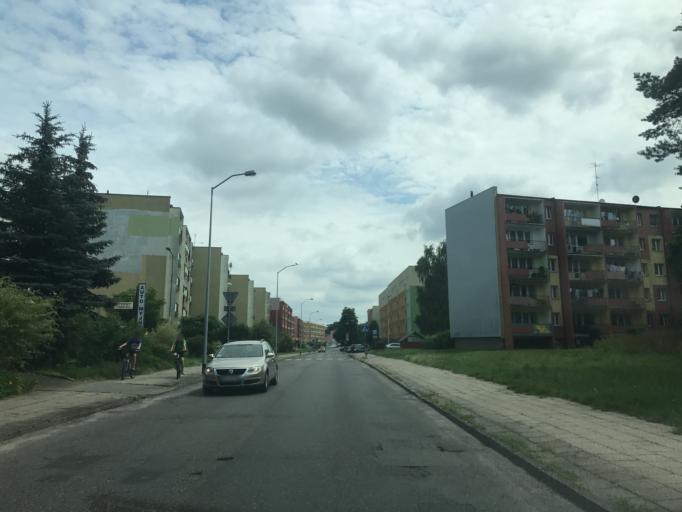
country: PL
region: West Pomeranian Voivodeship
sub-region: Powiat goleniowski
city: Goleniow
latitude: 53.5651
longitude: 14.8163
